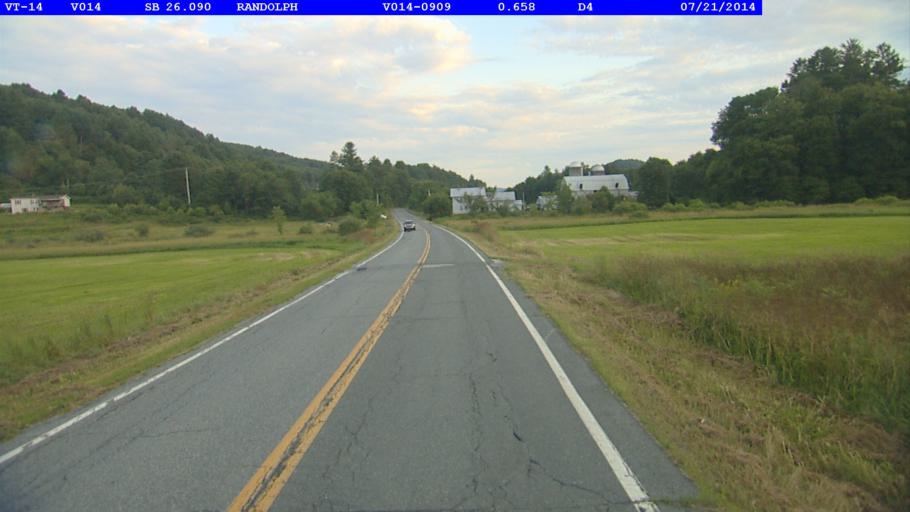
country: US
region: Vermont
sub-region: Orange County
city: Randolph
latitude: 43.8852
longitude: -72.5813
